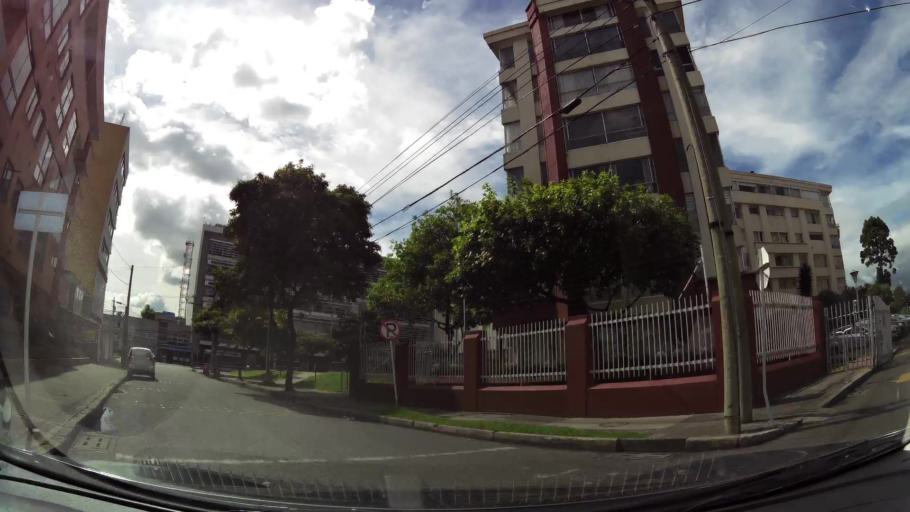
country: CO
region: Bogota D.C.
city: Barrio San Luis
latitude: 4.6847
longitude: -74.0597
